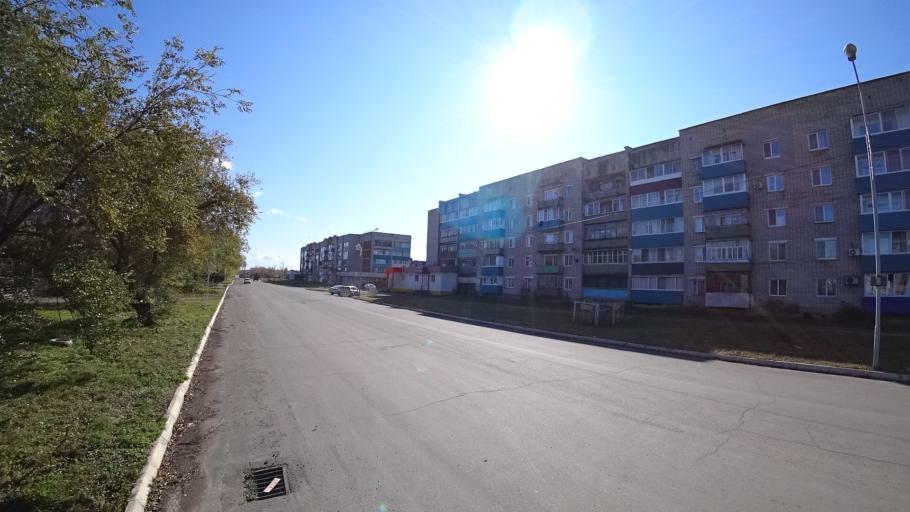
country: RU
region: Khabarovsk Krai
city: Amursk
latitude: 50.0998
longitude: 136.5146
